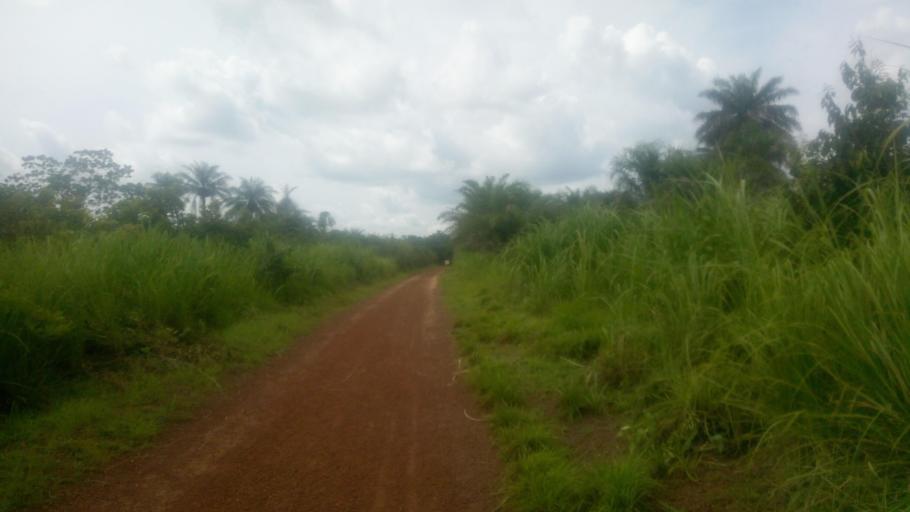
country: SL
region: Northern Province
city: Magburaka
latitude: 8.6843
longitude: -12.0660
